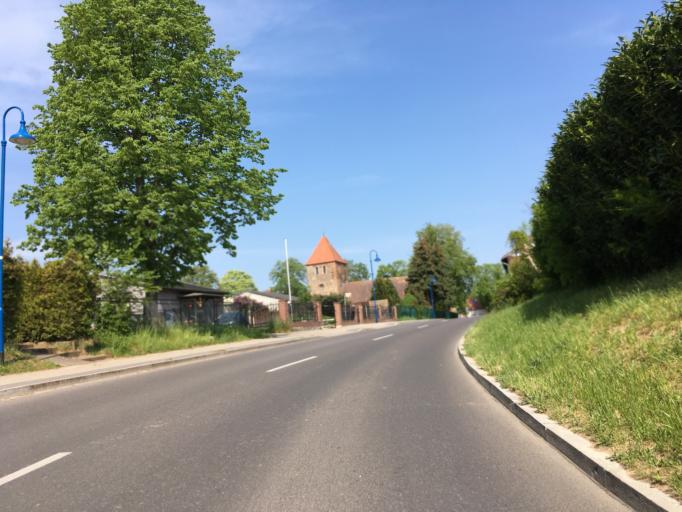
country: DE
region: Brandenburg
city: Werneuchen
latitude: 52.6492
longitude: 13.7236
